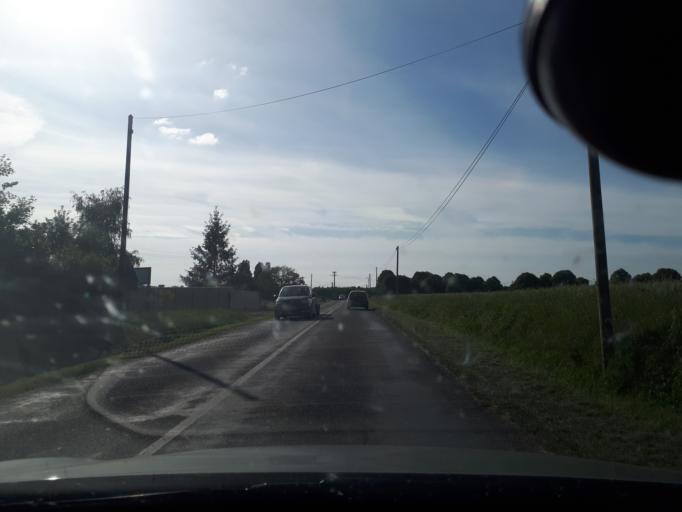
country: FR
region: Pays de la Loire
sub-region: Departement de la Sarthe
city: Champagne
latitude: 48.0804
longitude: 0.3216
